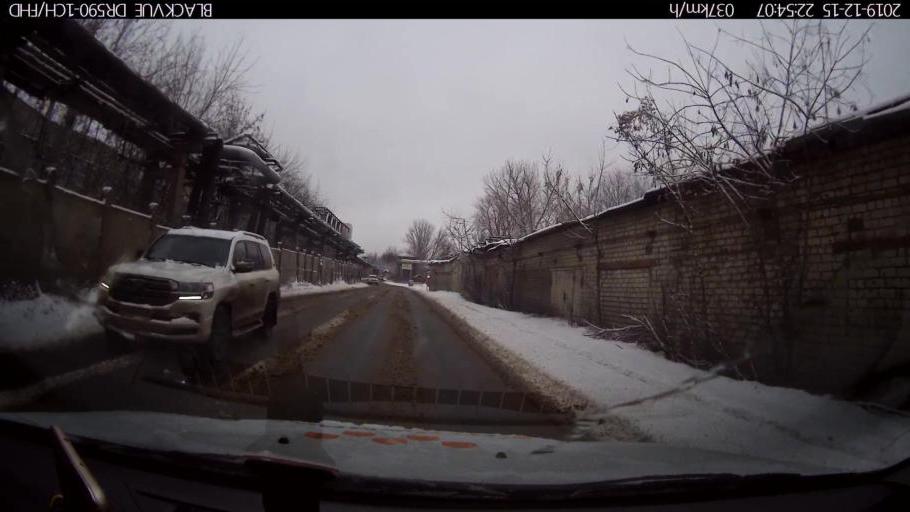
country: RU
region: Nizjnij Novgorod
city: Neklyudovo
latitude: 56.3538
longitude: 43.8796
